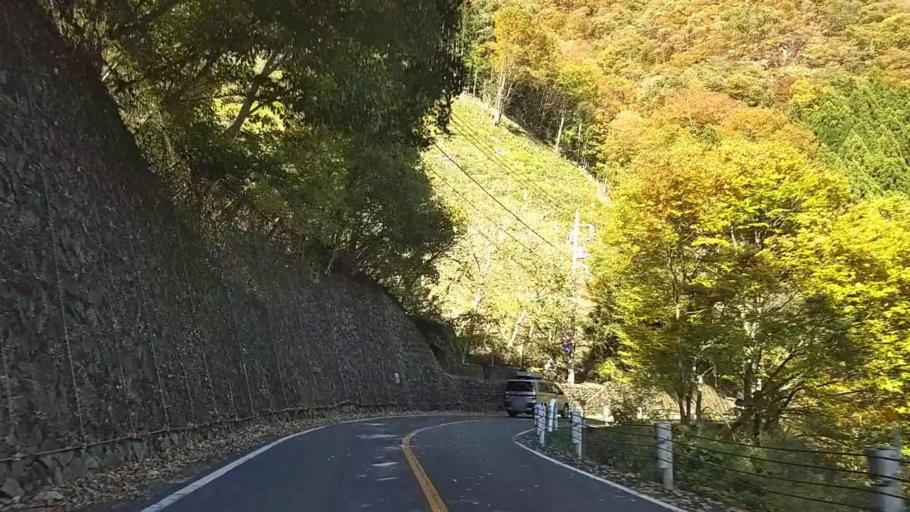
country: JP
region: Yamanashi
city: Otsuki
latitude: 35.7666
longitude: 138.9936
